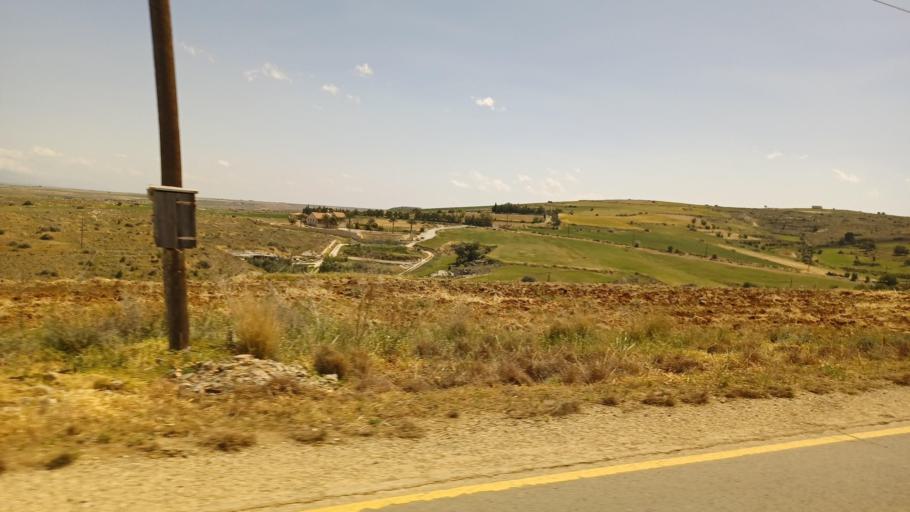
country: CY
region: Lefkosia
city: Astromeritis
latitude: 35.0862
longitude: 33.0149
